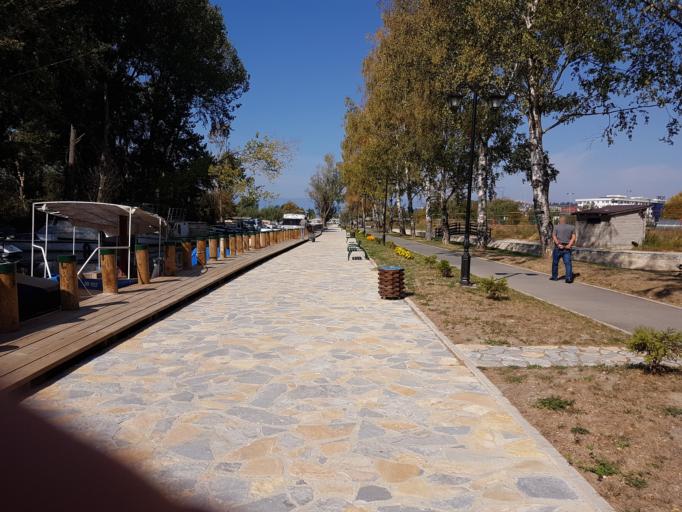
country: MK
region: Ohrid
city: Ohrid
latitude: 41.1027
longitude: 20.8133
